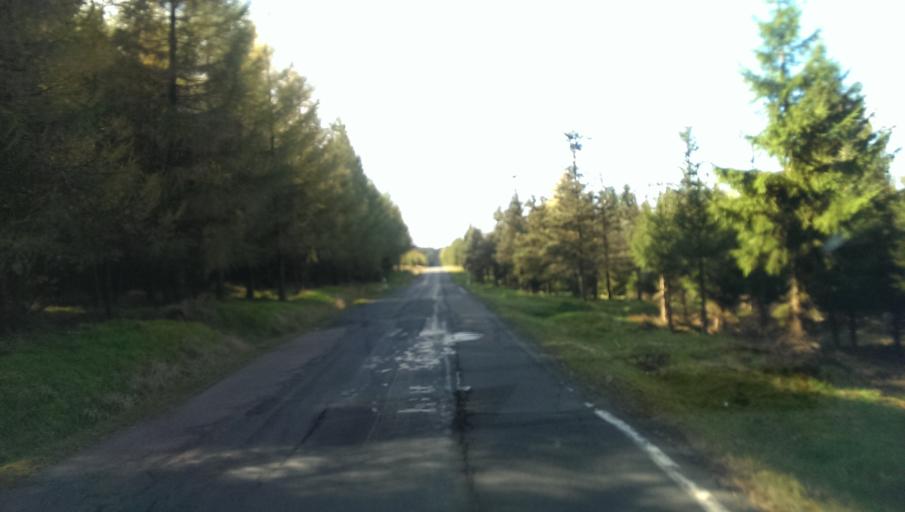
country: DE
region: Saxony
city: Altenberg
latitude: 50.7522
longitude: 13.7228
